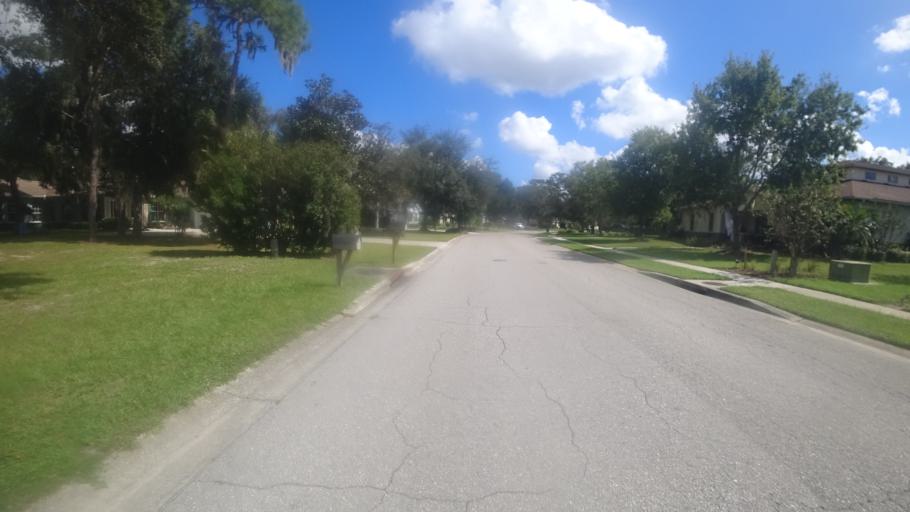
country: US
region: Florida
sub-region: Manatee County
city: Ellenton
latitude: 27.5112
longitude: -82.4030
